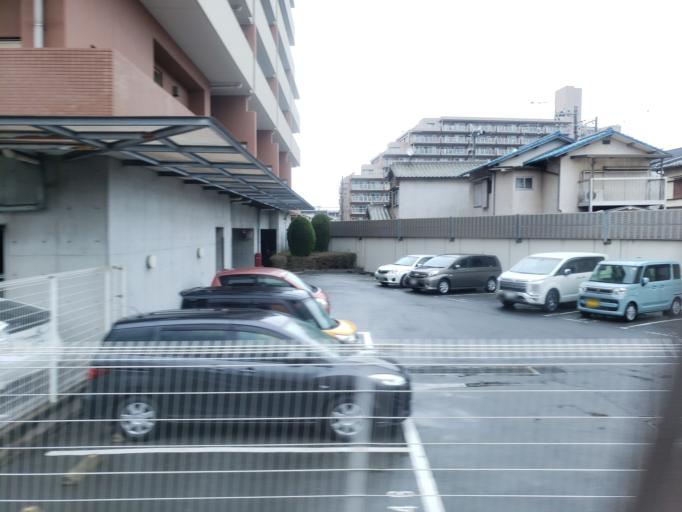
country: JP
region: Hyogo
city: Kakogawacho-honmachi
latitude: 34.7158
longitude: 134.8690
